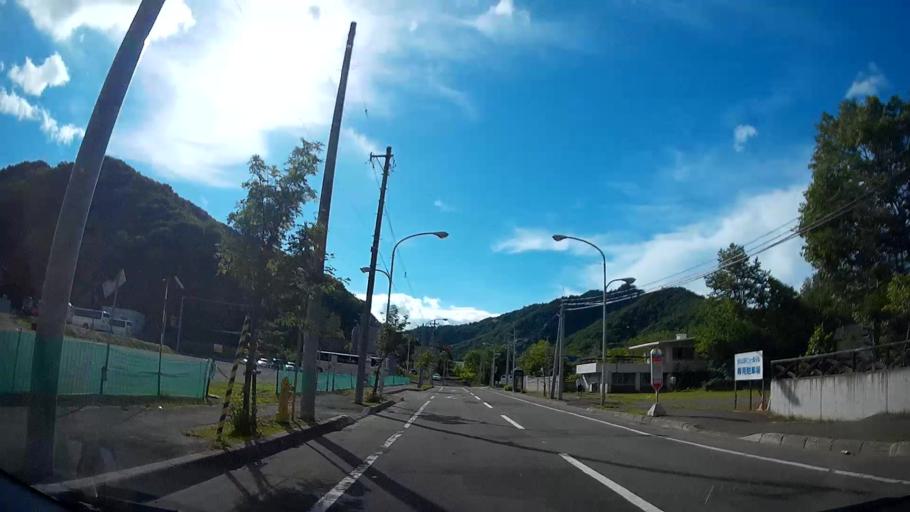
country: JP
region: Hokkaido
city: Sapporo
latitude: 42.9696
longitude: 141.1651
